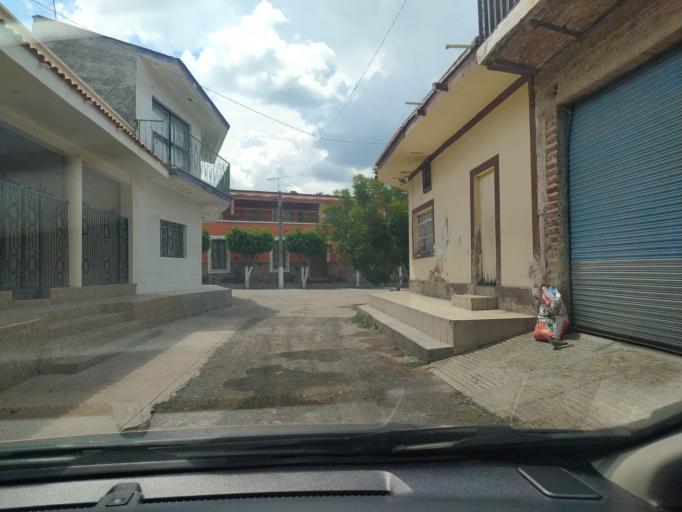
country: MX
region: Jalisco
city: Villa Corona
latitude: 20.3512
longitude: -103.6715
